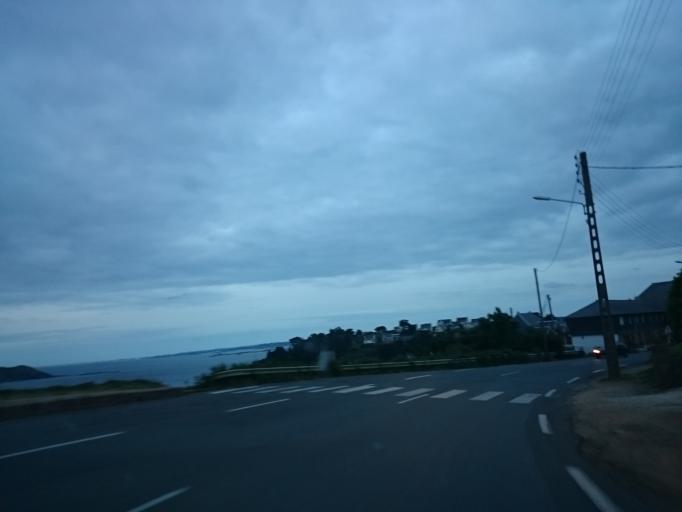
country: FR
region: Brittany
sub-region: Departement des Cotes-d'Armor
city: Perros-Guirec
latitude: 48.8192
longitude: -3.4368
